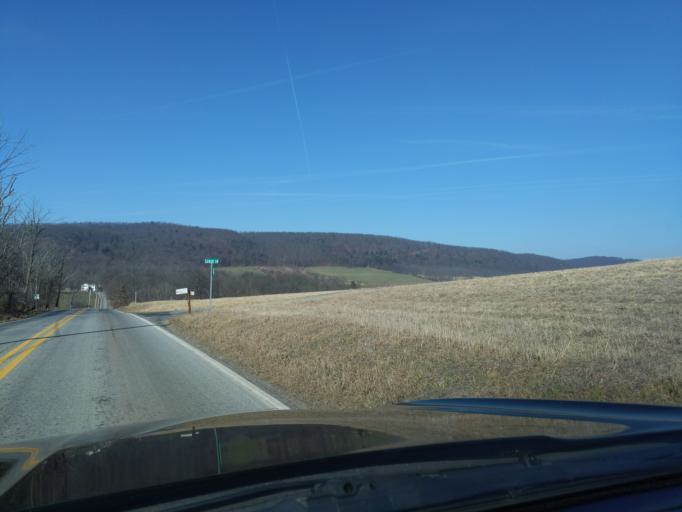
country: US
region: Pennsylvania
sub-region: Blair County
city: Tipton
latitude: 40.6149
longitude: -78.2583
